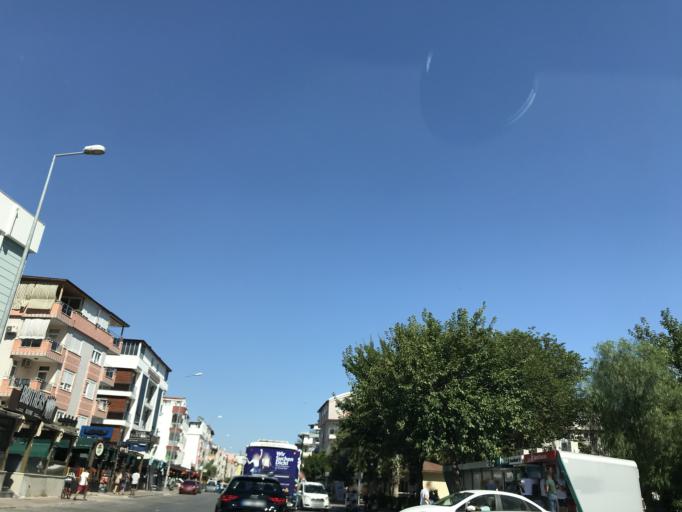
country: TR
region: Antalya
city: Antalya
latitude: 36.9028
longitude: 30.6559
